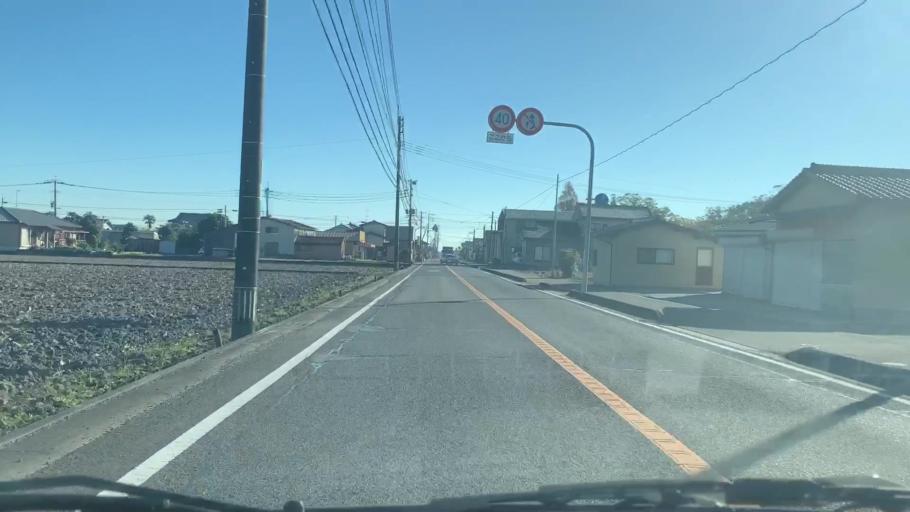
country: JP
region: Saga Prefecture
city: Kashima
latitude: 33.1836
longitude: 130.1703
